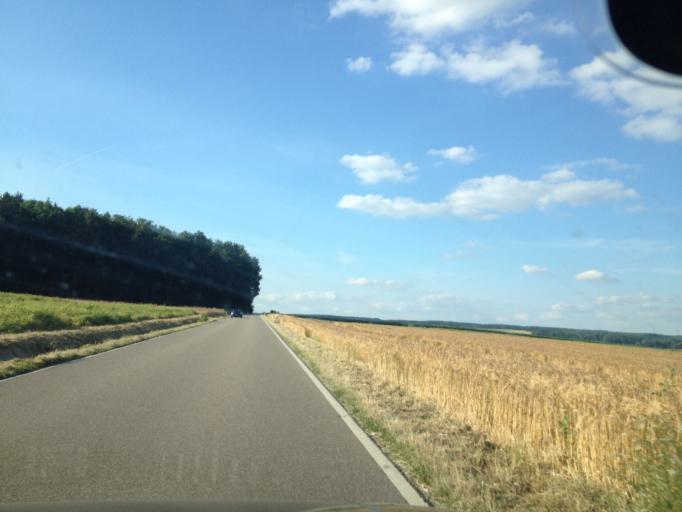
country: DE
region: Baden-Wuerttemberg
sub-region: Regierungsbezirk Stuttgart
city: Neuenstadt am Kocher
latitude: 49.2317
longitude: 9.3067
